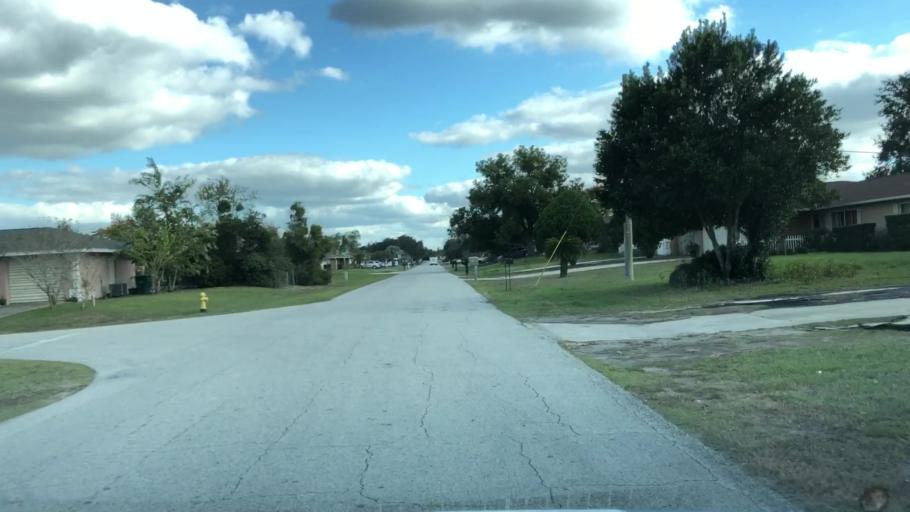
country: US
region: Florida
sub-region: Volusia County
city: Deltona
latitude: 28.8804
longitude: -81.2408
